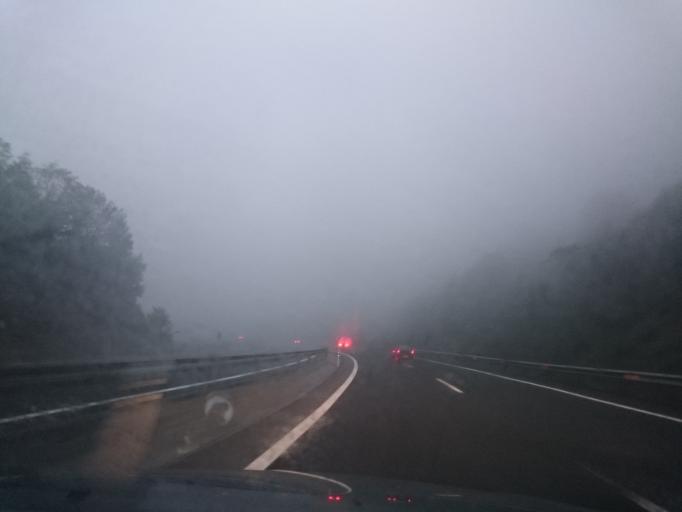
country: ES
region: Asturias
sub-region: Province of Asturias
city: Pola de Lena
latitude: 43.0174
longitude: -5.8157
